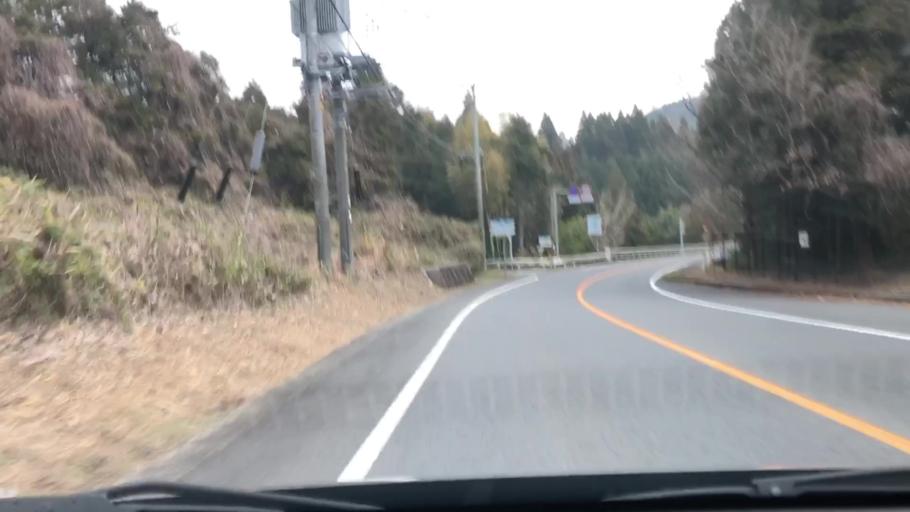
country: JP
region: Oita
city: Usuki
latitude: 33.0092
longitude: 131.6342
